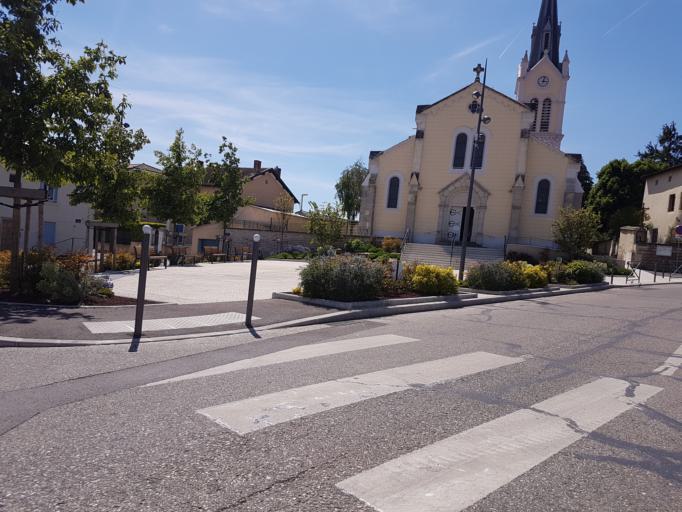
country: FR
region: Rhone-Alpes
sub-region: Departement du Rhone
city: Jonage
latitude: 45.7958
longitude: 5.0473
